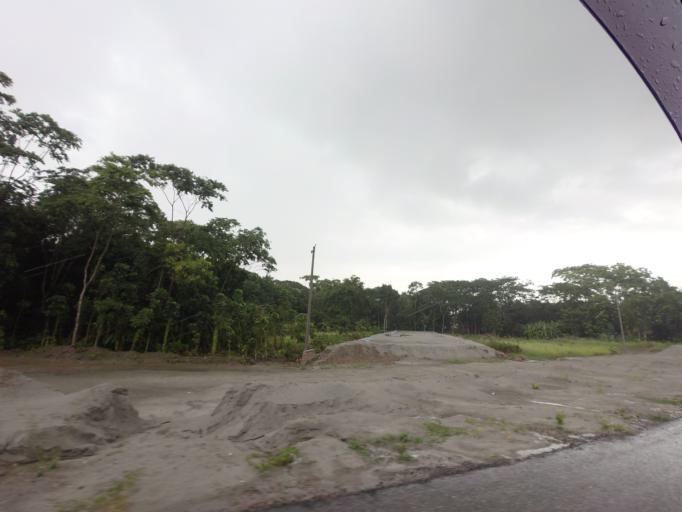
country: BD
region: Dhaka
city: Char Bhadrasan
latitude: 23.3754
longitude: 90.1025
